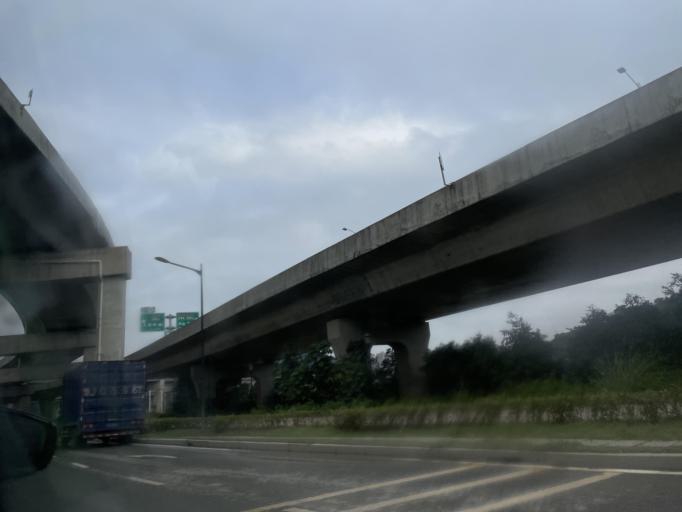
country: CN
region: Guangdong
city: Nanping
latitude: 22.1767
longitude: 113.4650
